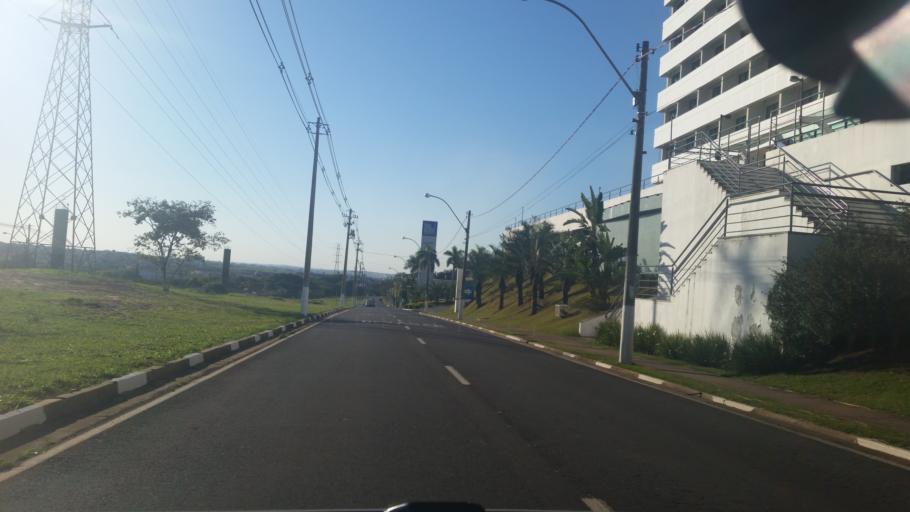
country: BR
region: Sao Paulo
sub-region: Campinas
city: Campinas
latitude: -22.8573
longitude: -47.0552
